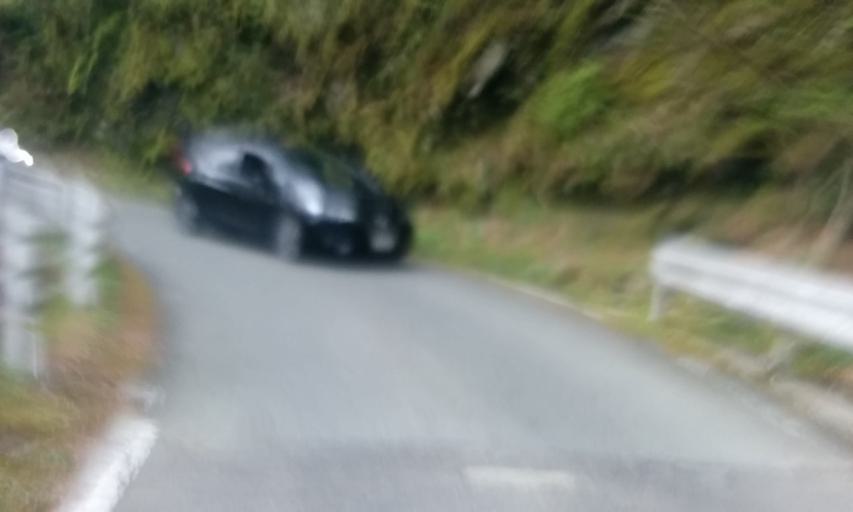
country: JP
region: Ehime
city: Saijo
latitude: 33.7927
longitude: 133.2685
